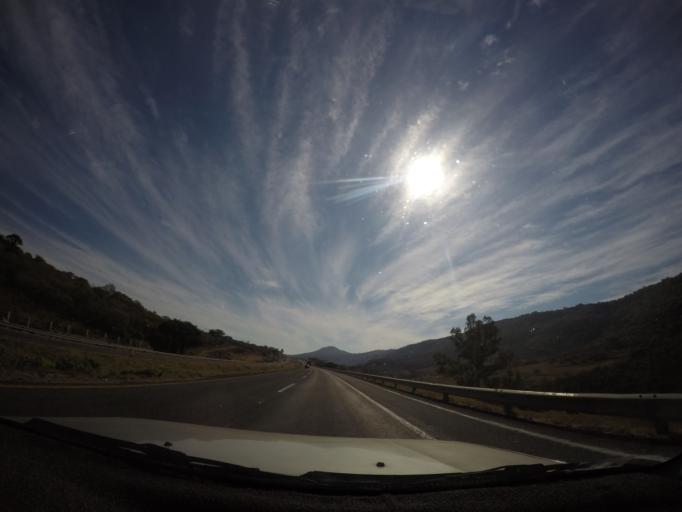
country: MX
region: Jalisco
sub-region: Zapotlan del Rey
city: Zapotlan del Rey
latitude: 20.5056
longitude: -102.9610
